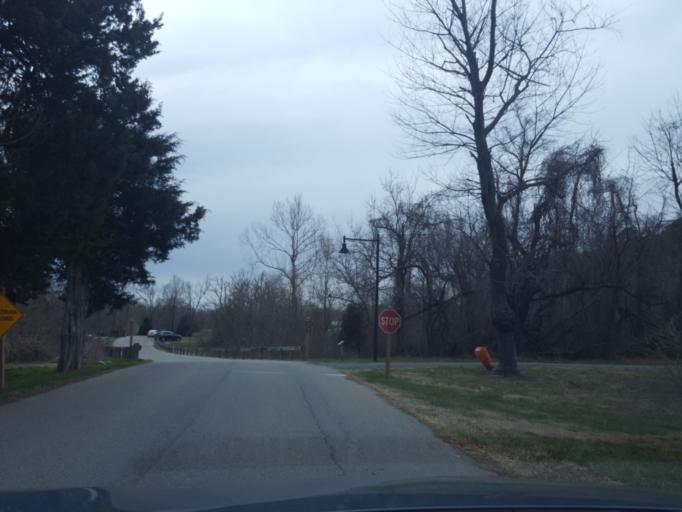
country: US
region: Maryland
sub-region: Calvert County
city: Lusby
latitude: 38.4004
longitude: -76.5091
